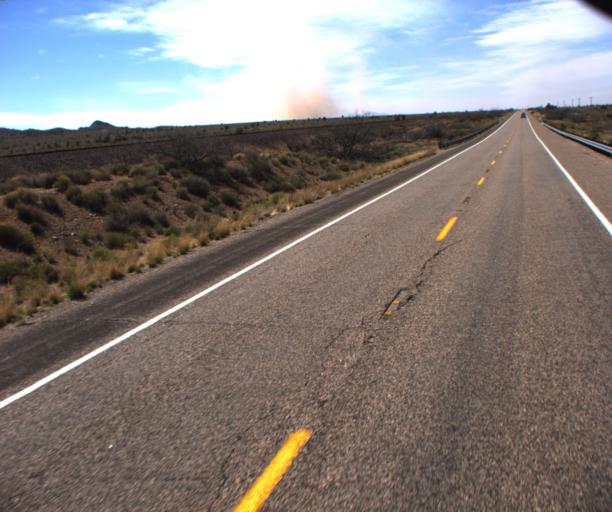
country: US
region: Arizona
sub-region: Mohave County
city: New Kingman-Butler
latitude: 35.4036
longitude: -113.7650
